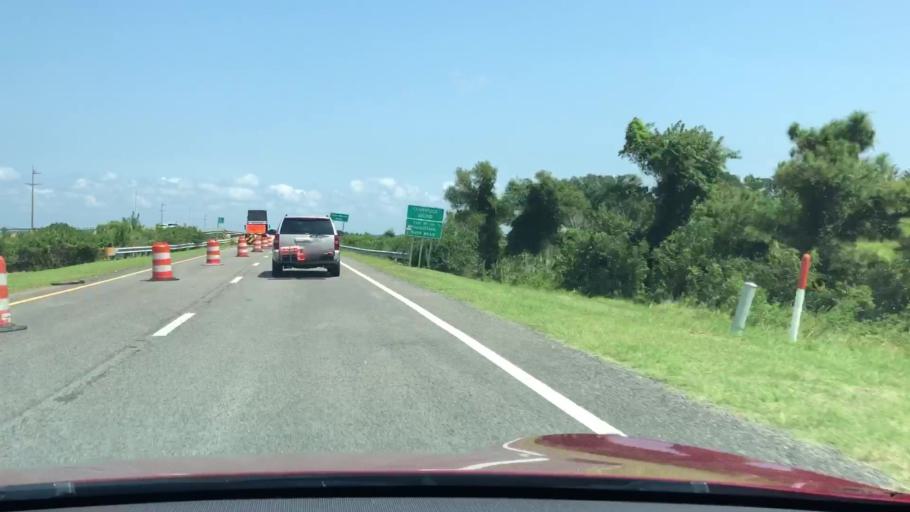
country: US
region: North Carolina
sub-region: Dare County
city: Southern Shores
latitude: 36.0801
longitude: -75.7909
